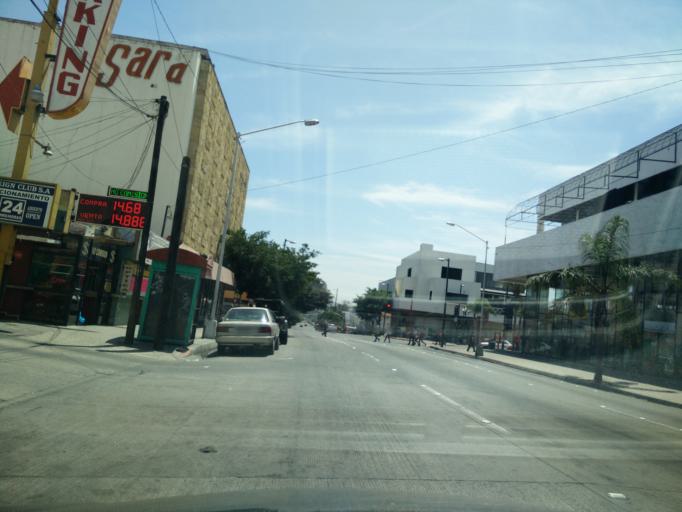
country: MX
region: Baja California
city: Tijuana
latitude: 32.5328
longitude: -117.0374
